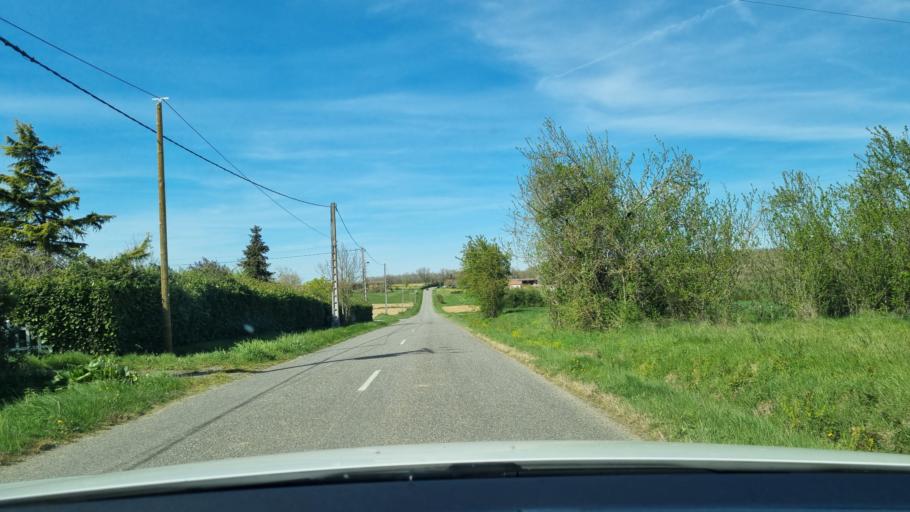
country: FR
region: Midi-Pyrenees
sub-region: Departement de la Haute-Garonne
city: Rieumes
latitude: 43.4725
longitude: 1.0632
